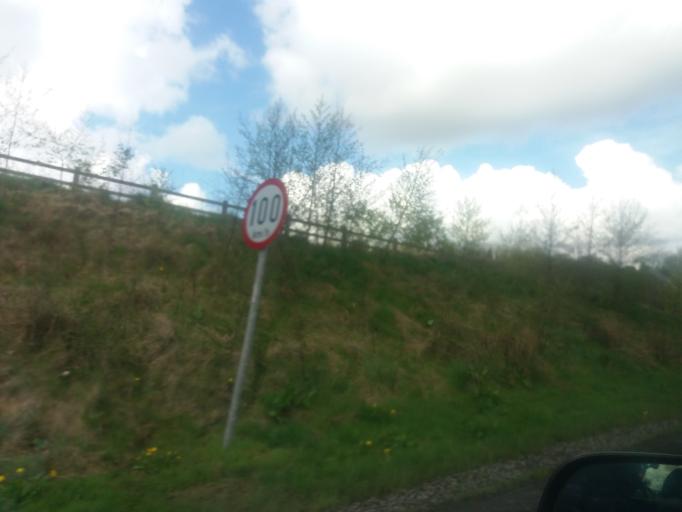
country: IE
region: Ulster
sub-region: An Cabhan
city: Belturbet
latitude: 54.0700
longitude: -7.4085
